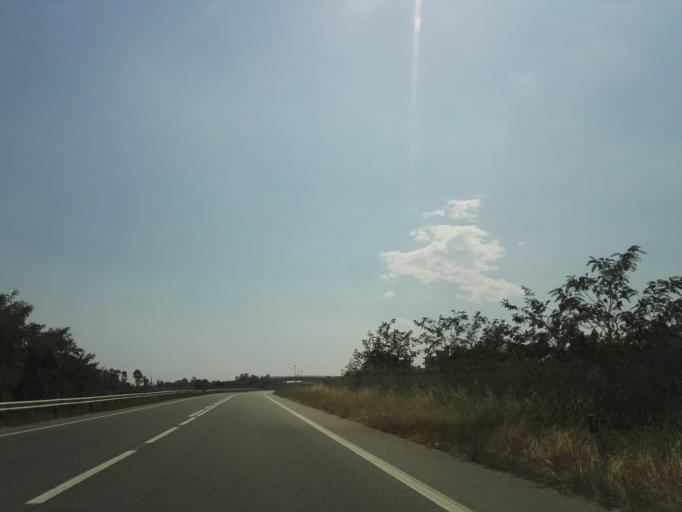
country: IT
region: Calabria
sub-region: Provincia di Reggio Calabria
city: Caulonia Marina
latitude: 38.3624
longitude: 16.4951
